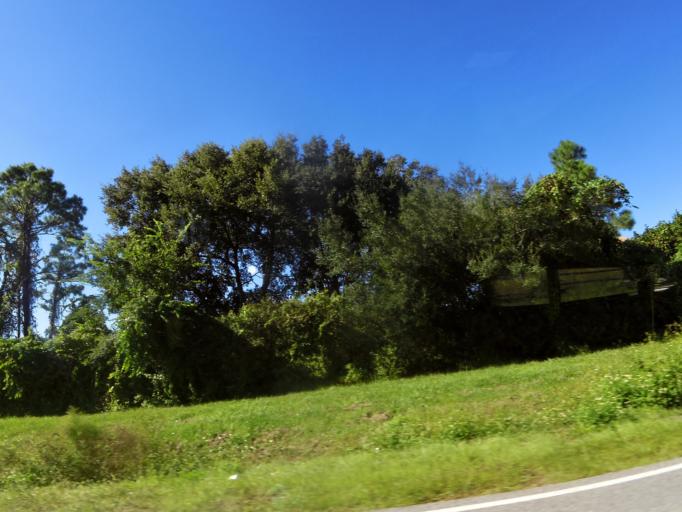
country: US
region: Florida
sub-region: Saint Johns County
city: Palm Valley
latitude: 30.1565
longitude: -81.3729
